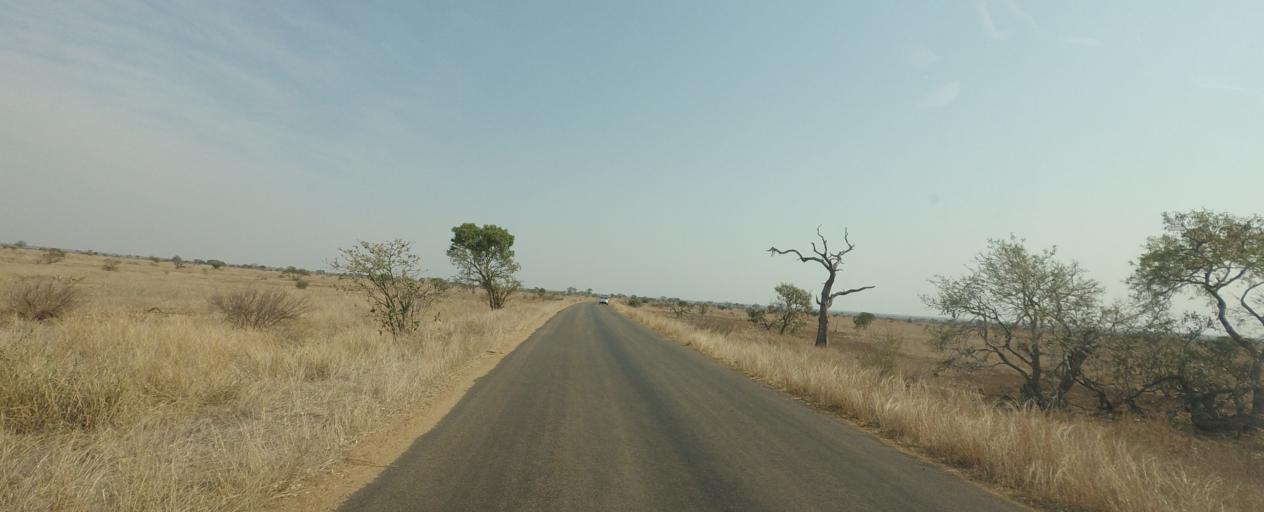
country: ZA
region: Limpopo
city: Thulamahashi
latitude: -24.3215
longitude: 31.7508
